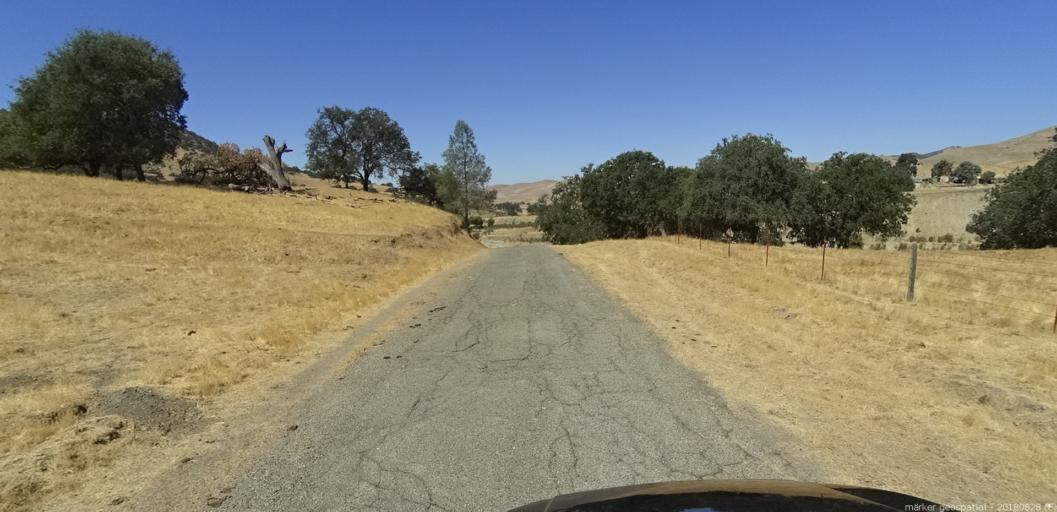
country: US
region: California
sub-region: San Luis Obispo County
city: San Miguel
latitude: 36.0654
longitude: -120.7632
